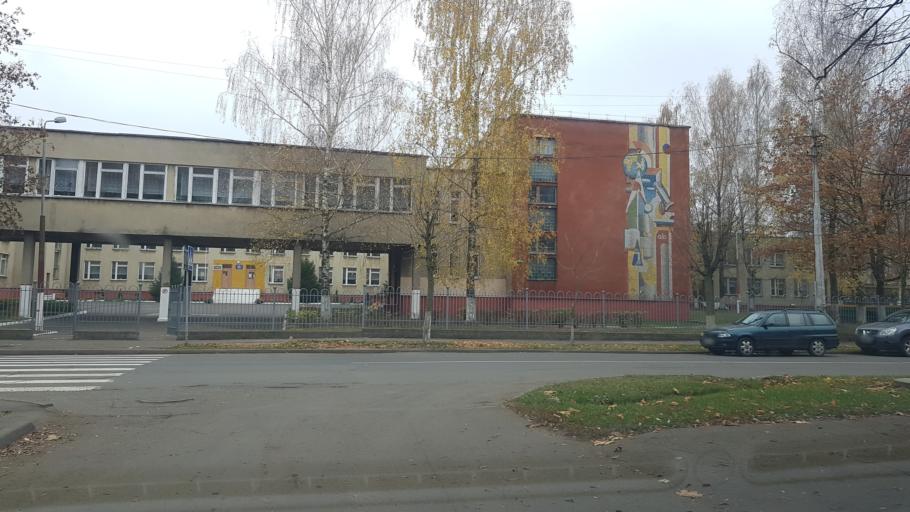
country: BY
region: Mogilev
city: Babruysk
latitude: 53.1512
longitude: 29.2408
